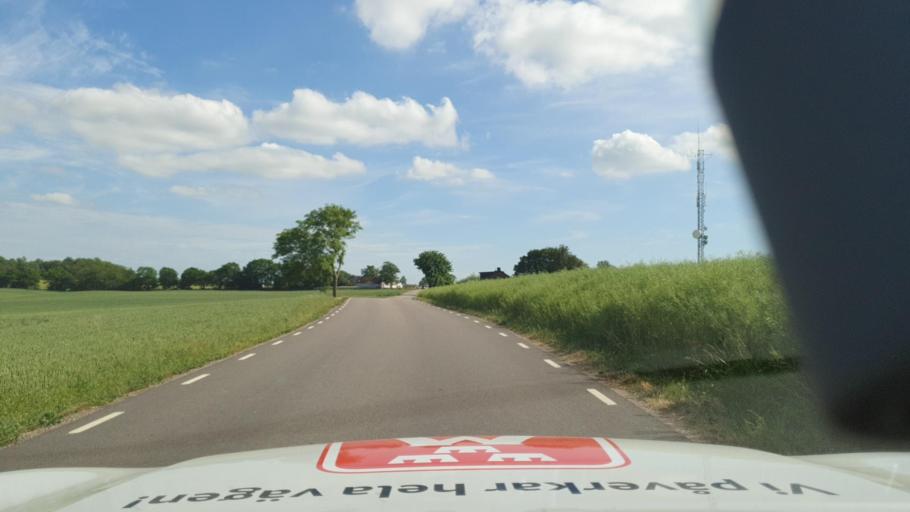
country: SE
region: Skane
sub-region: Sjobo Kommun
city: Blentarp
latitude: 55.5486
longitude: 13.5590
